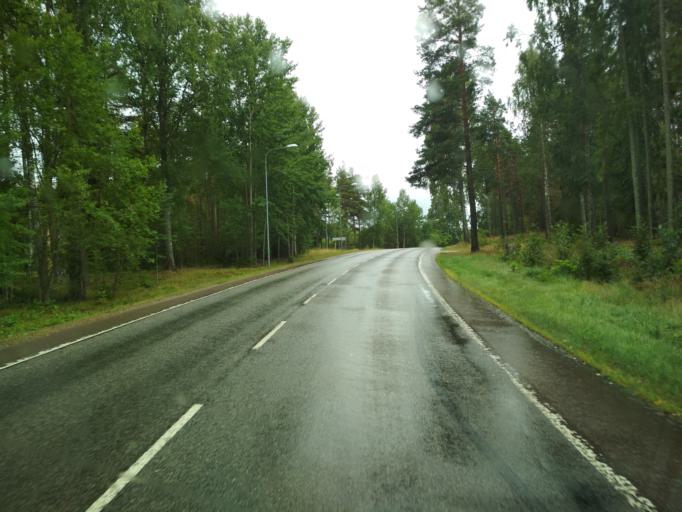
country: SE
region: Vaestmanland
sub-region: Surahammars Kommun
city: Ramnas
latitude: 59.7695
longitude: 16.2028
